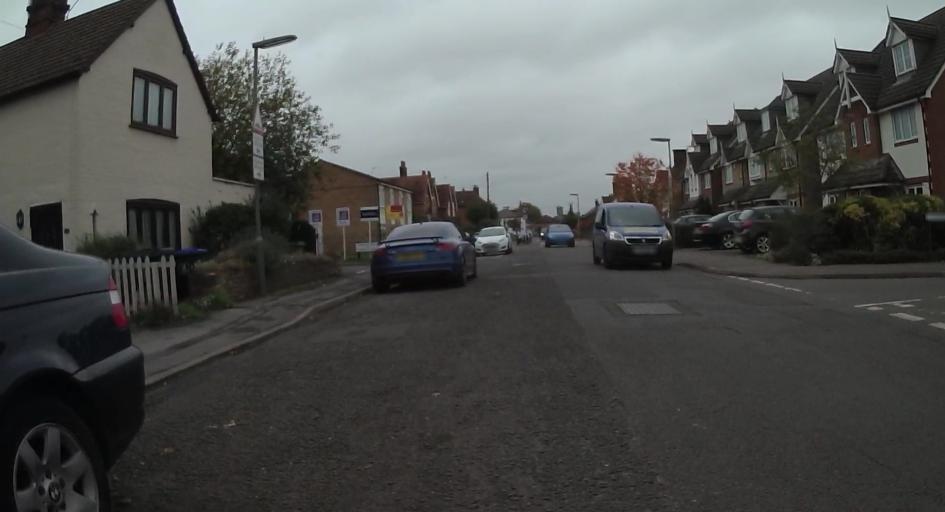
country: GB
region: England
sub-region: Surrey
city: Byfleet
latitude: 51.3425
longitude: -0.4807
